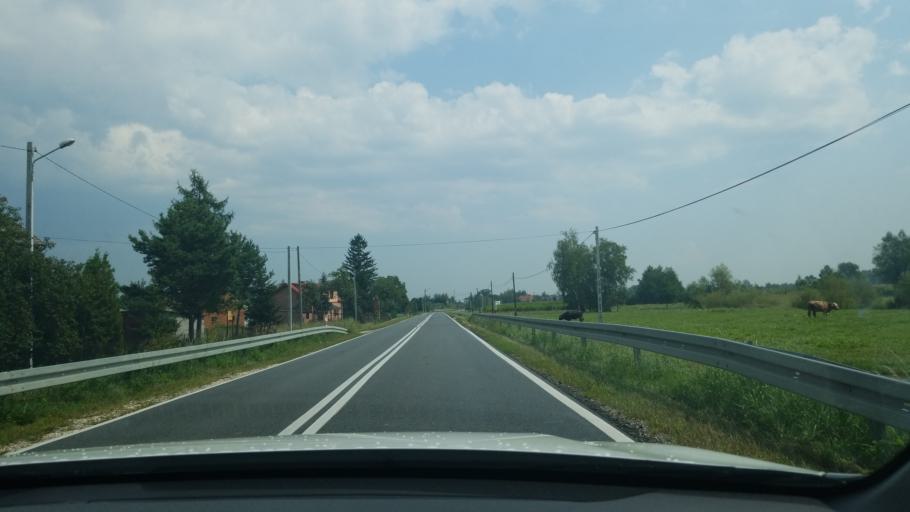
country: PL
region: Lesser Poland Voivodeship
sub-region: Powiat bochenski
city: Dziewin
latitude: 50.1226
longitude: 20.4786
